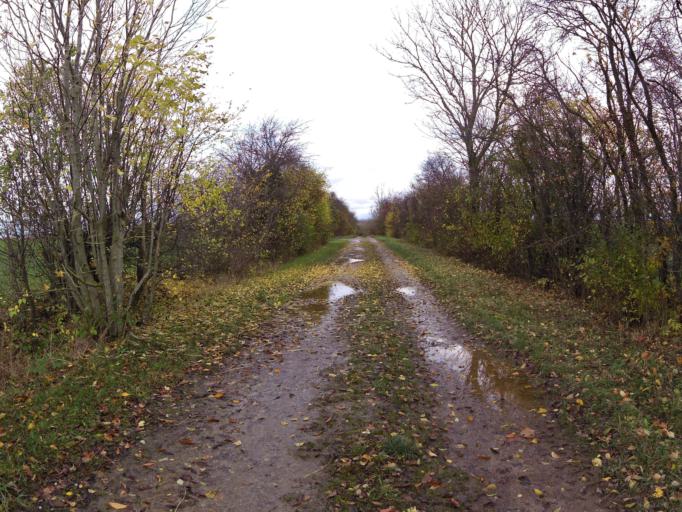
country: DE
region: Thuringia
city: Ifta
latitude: 51.0571
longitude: 10.1312
